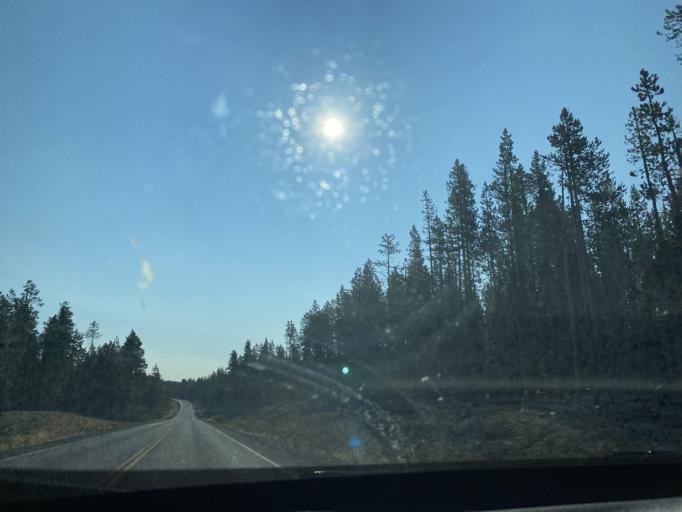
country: US
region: Oregon
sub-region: Deschutes County
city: Three Rivers
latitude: 43.7045
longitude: -121.2533
